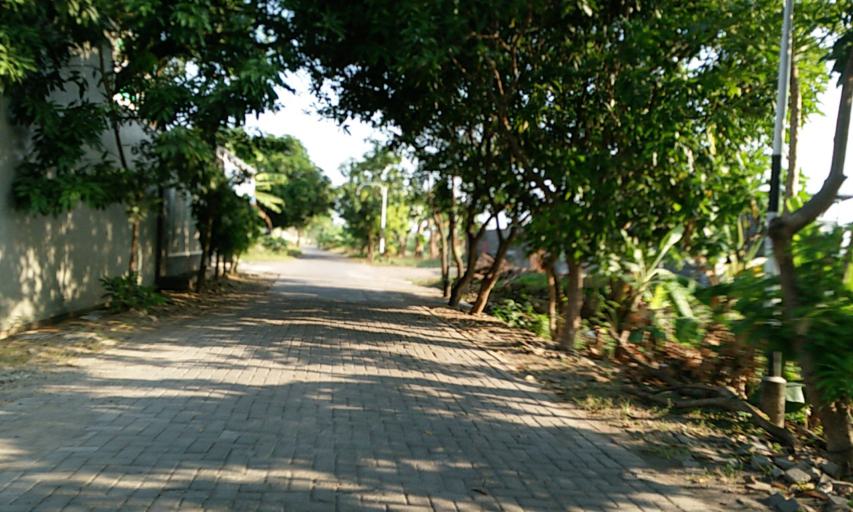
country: ID
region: Central Java
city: Mranggen
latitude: -7.0082
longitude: 110.4871
